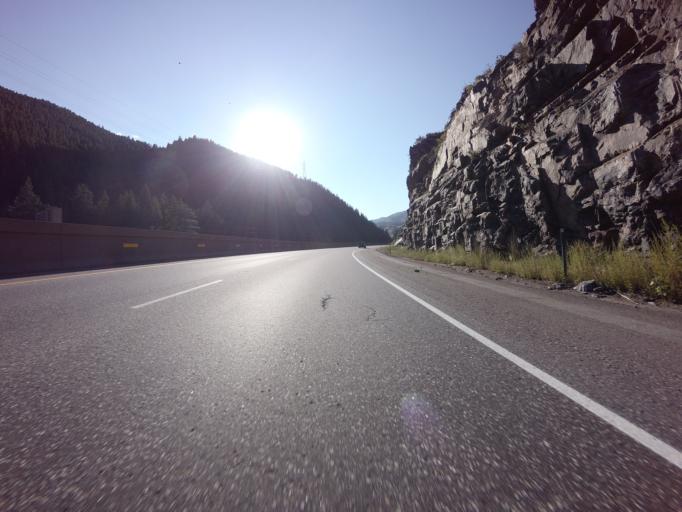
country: US
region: Colorado
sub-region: Clear Creek County
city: Idaho Springs
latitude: 39.7435
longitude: -105.4537
